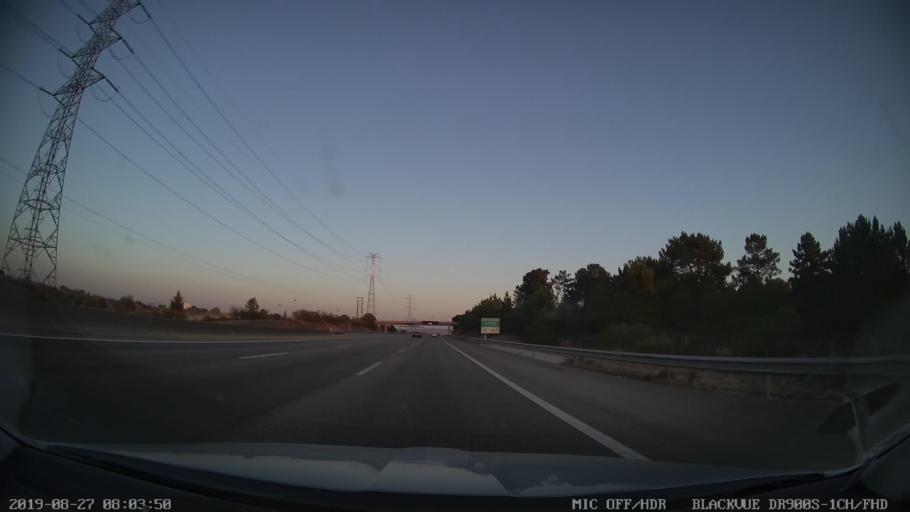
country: PT
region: Setubal
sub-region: Seixal
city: Aldeia de Paio Pires
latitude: 38.5956
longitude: -9.0762
